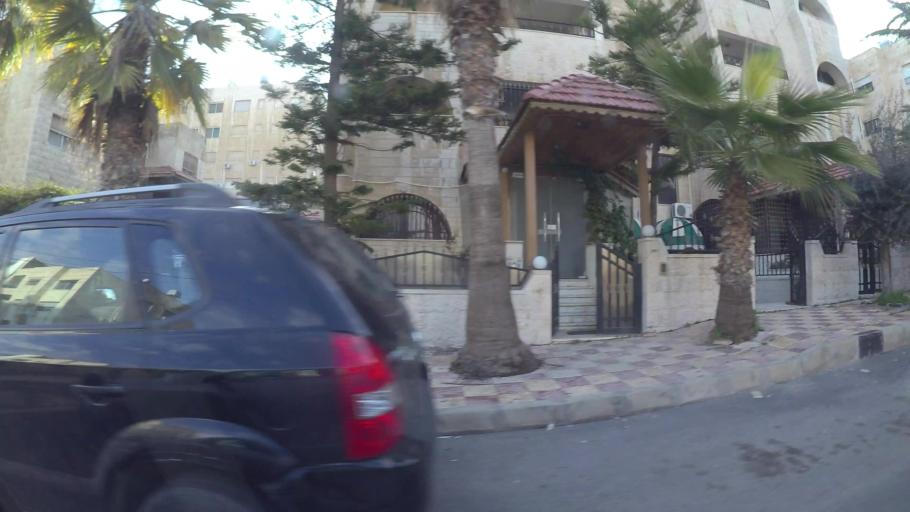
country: JO
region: Amman
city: Al Jubayhah
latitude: 32.0019
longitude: 35.8695
